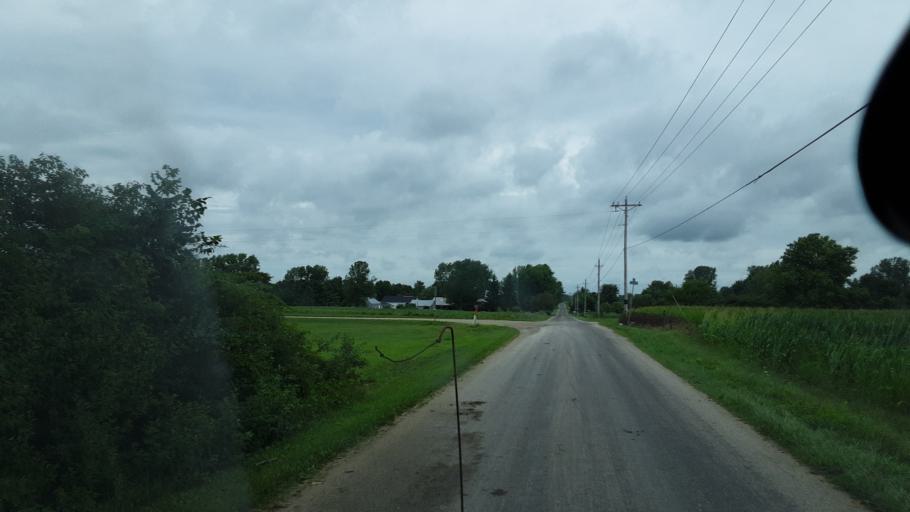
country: US
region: Indiana
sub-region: Adams County
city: Geneva
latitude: 40.5209
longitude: -85.0100
